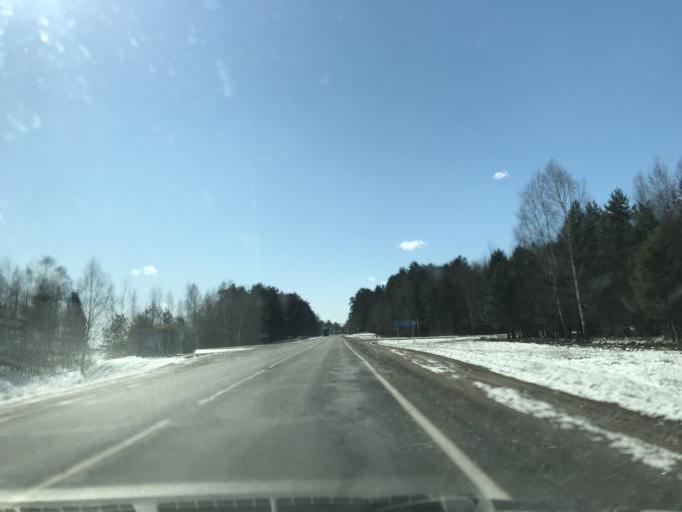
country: BY
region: Mogilev
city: Poselok Voskhod
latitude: 53.6850
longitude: 30.3696
